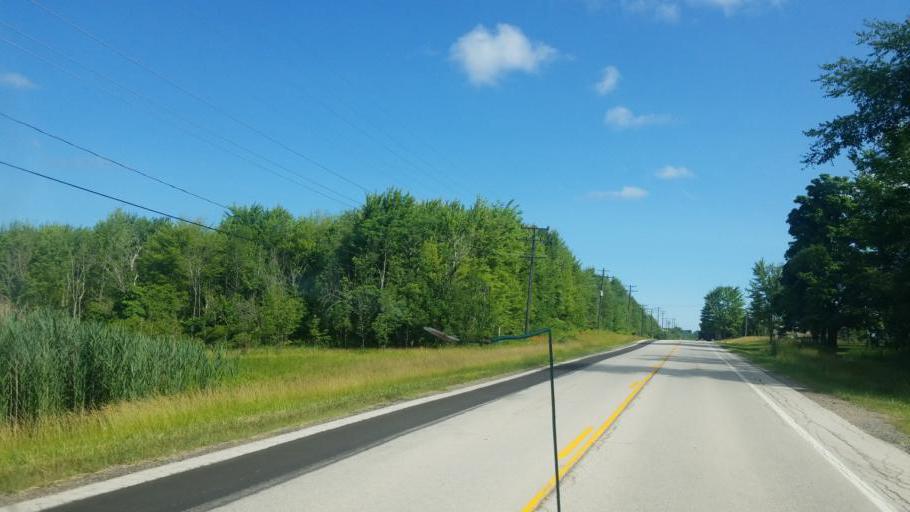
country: US
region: Ohio
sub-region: Ashtabula County
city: Conneaut
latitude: 41.8768
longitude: -80.5723
